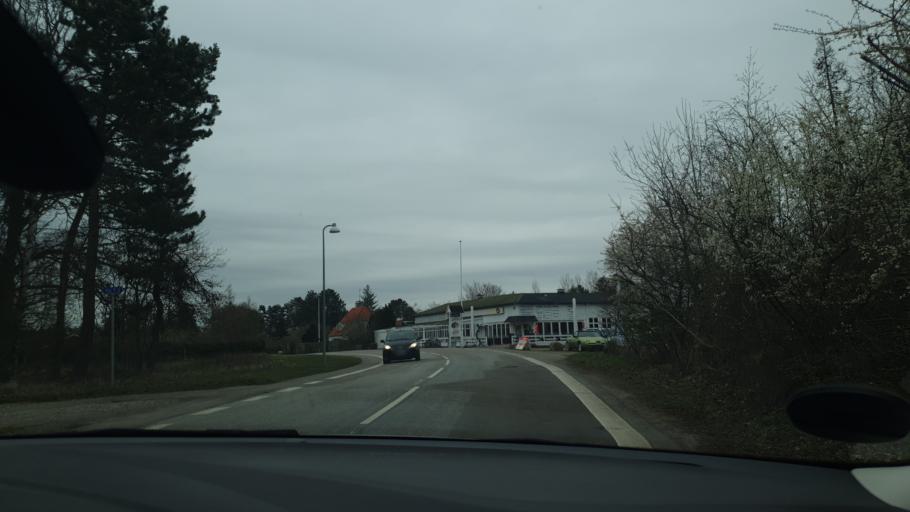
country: DK
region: Zealand
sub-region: Odsherred Kommune
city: Asnaes
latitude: 55.8541
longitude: 11.5203
